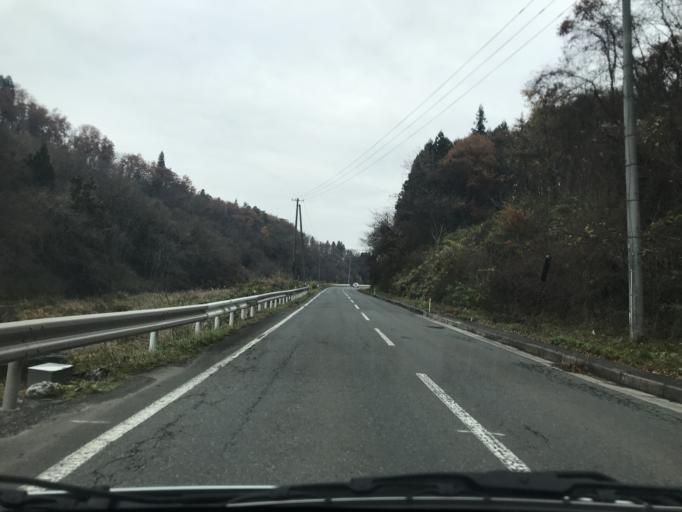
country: JP
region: Iwate
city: Mizusawa
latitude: 39.1831
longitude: 141.2211
